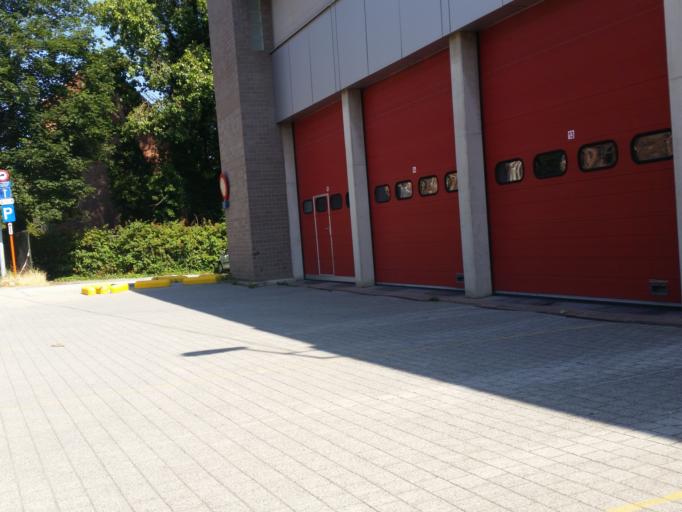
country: BE
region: Flanders
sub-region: Provincie Antwerpen
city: Mechelen
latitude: 51.0274
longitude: 4.4677
